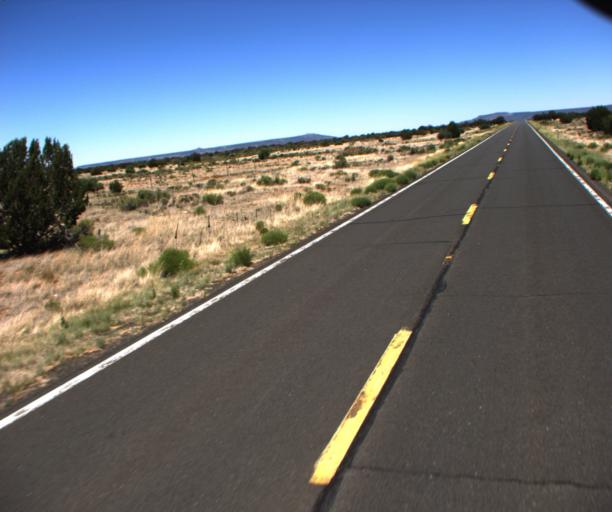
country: US
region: Arizona
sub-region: Coconino County
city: LeChee
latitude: 34.7427
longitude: -111.0520
